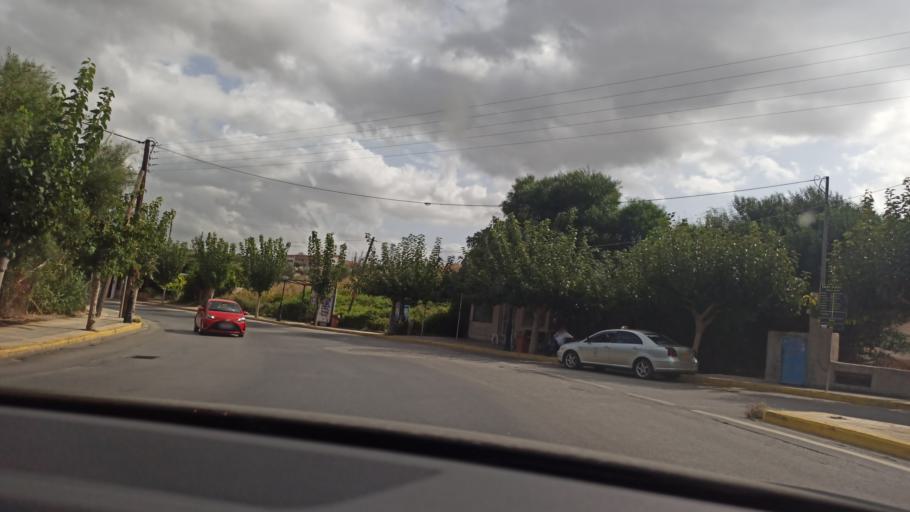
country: GR
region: Crete
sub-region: Nomos Irakleiou
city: Gazi
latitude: 35.3349
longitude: 25.0572
